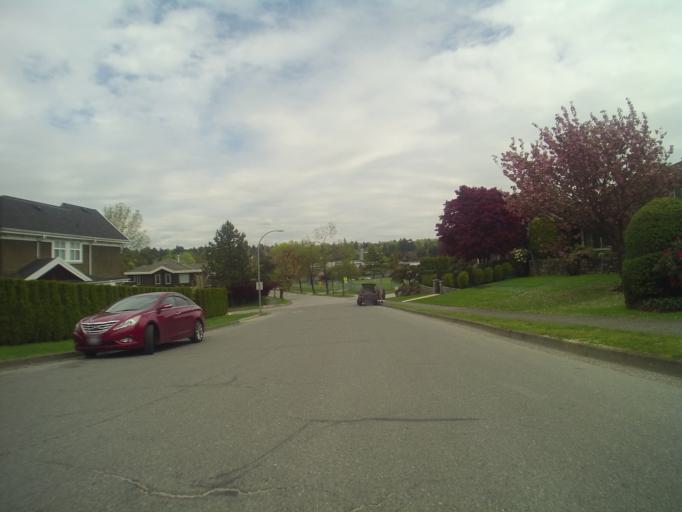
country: CA
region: British Columbia
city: Vancouver
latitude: 49.2451
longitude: -123.1612
